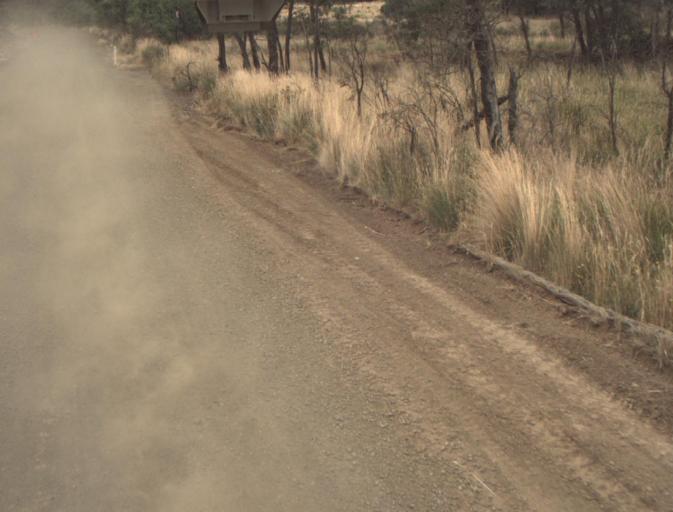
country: AU
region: Tasmania
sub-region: Northern Midlands
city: Evandale
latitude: -41.5152
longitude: 147.3506
